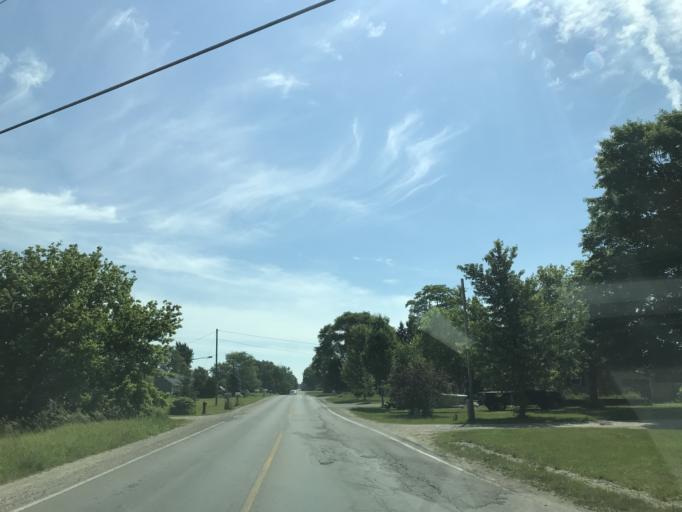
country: US
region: Michigan
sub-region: Grand Traverse County
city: Traverse City
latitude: 44.6576
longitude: -85.6669
